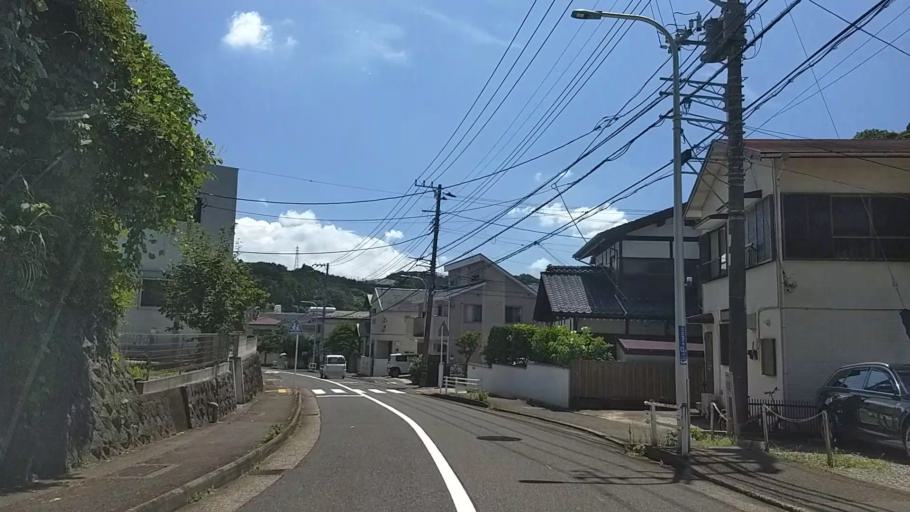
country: JP
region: Kanagawa
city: Zushi
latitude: 35.3004
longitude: 139.6008
